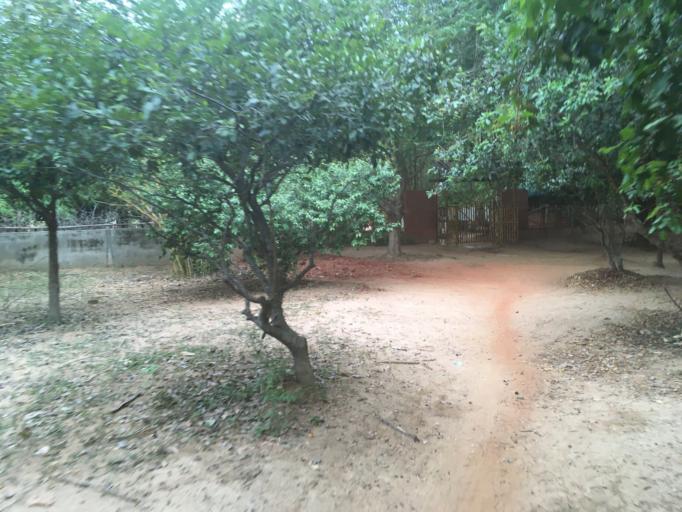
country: IN
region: Tamil Nadu
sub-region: Villupuram
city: Auroville
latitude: 12.0135
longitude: 79.8008
